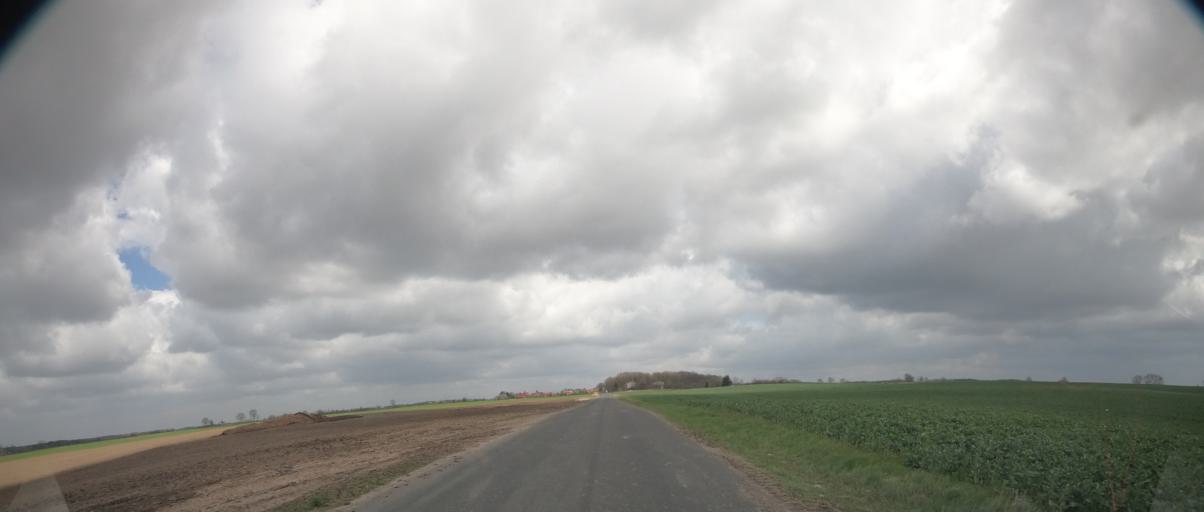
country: PL
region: West Pomeranian Voivodeship
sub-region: Powiat choszczenski
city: Recz
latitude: 53.2811
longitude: 15.4929
